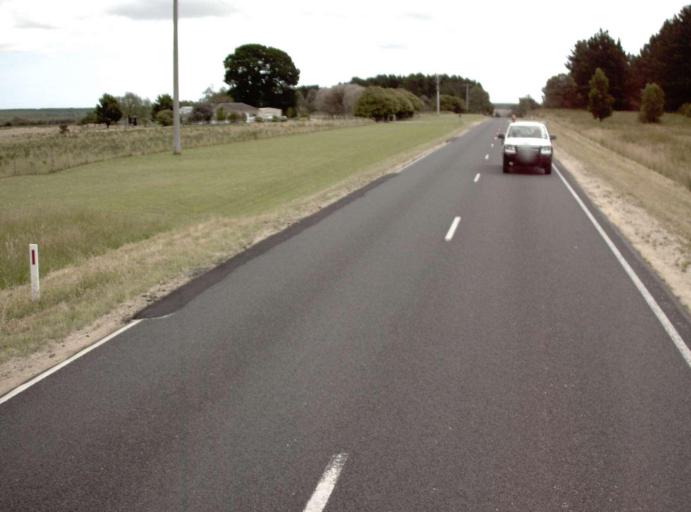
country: AU
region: Victoria
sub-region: Wellington
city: Sale
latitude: -38.1692
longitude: 147.0352
